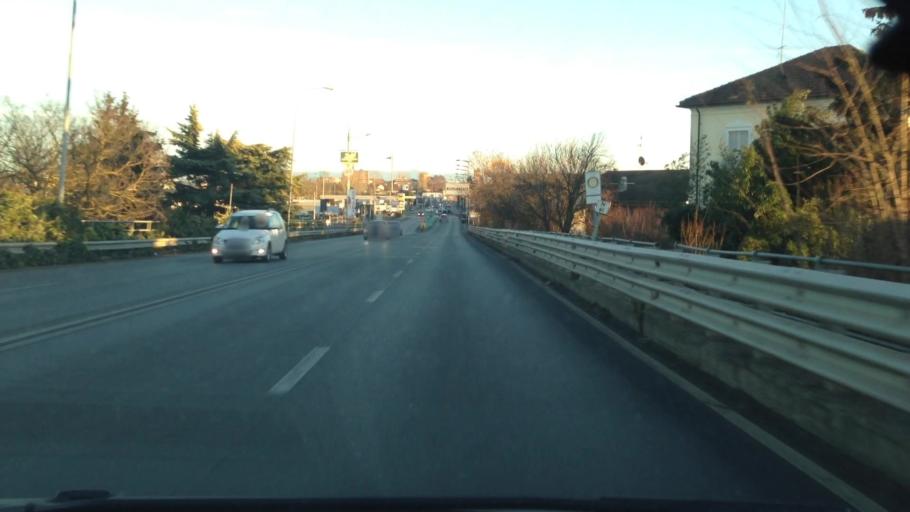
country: IT
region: Piedmont
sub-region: Provincia di Alessandria
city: Alessandria
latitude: 44.9219
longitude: 8.5899
